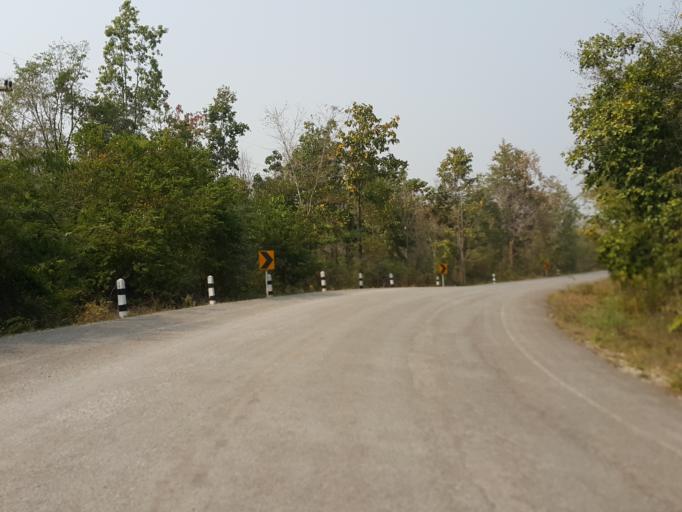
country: TH
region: Lampang
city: Mae Phrik
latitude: 17.4979
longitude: 99.0838
